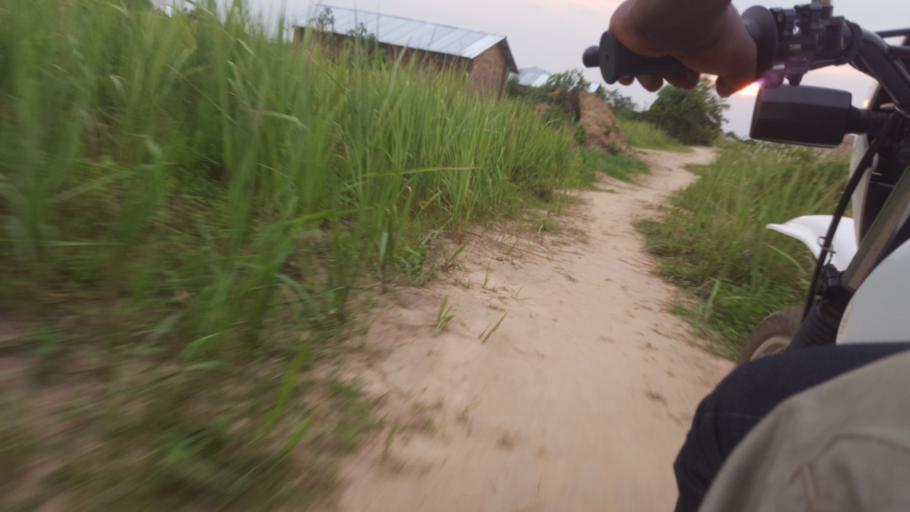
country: CD
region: Bandundu
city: Bandundu
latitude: -3.2809
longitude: 17.3878
